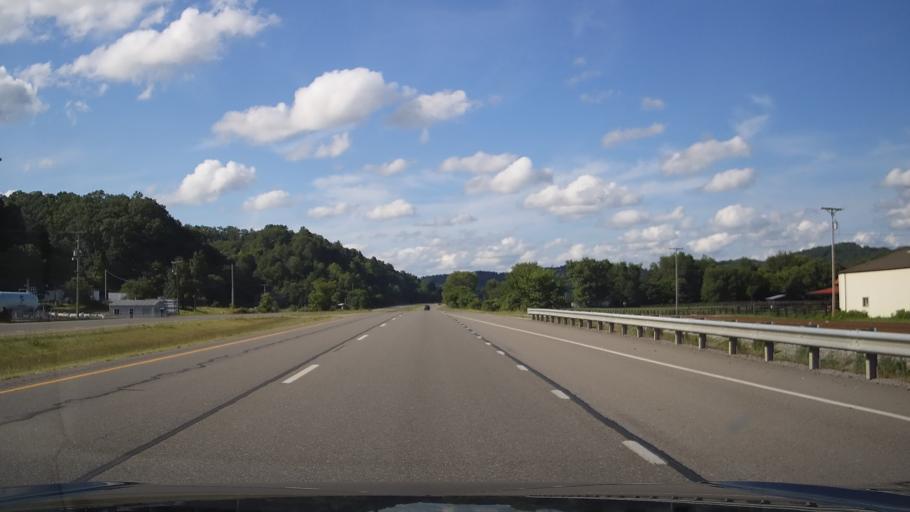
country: US
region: Kentucky
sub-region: Lawrence County
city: Louisa
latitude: 38.1947
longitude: -82.6053
